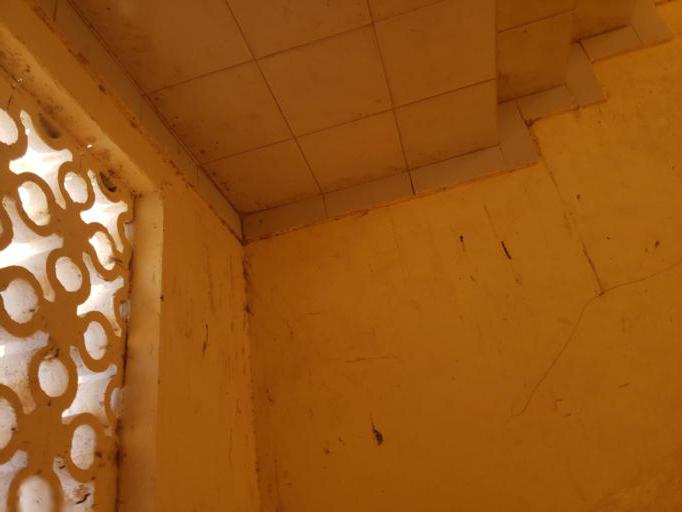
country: SN
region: Louga
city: Ndibene Dahra
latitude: 15.3998
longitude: -15.1328
